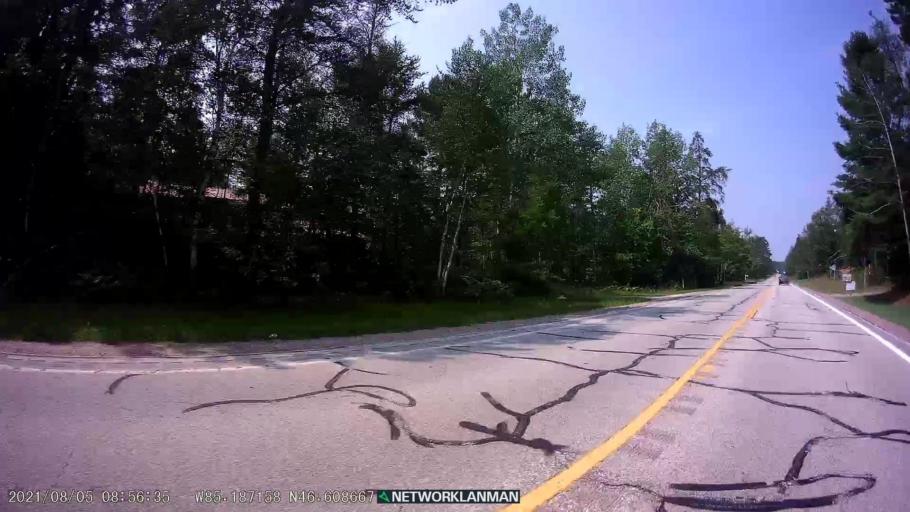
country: US
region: Michigan
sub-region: Luce County
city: Newberry
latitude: 46.6087
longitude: -85.1885
